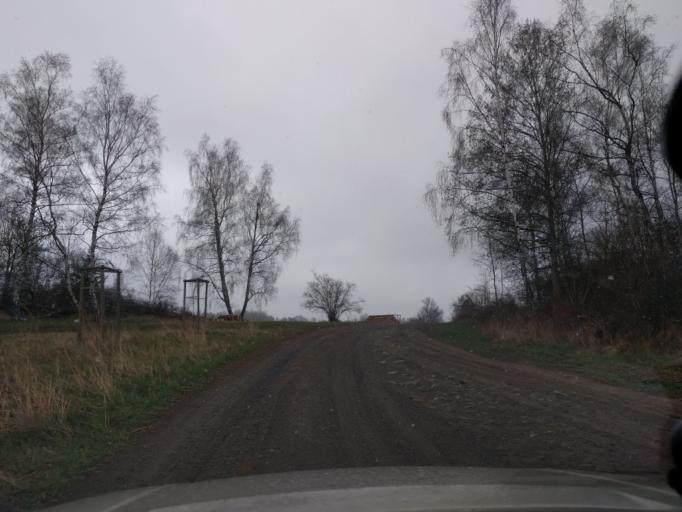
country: CZ
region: Karlovarsky
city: Bochov
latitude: 50.1051
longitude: 13.0950
